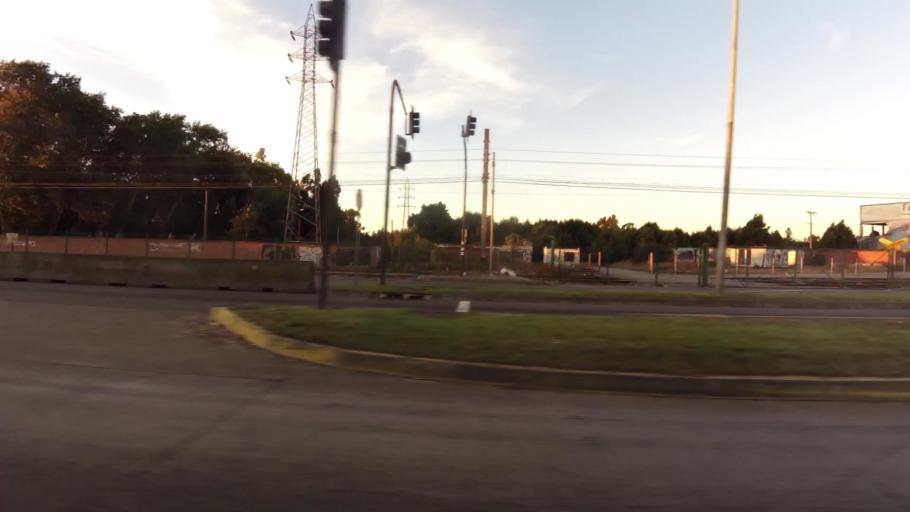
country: CL
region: Biobio
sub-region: Provincia de Concepcion
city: Concepcion
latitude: -36.8389
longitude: -73.0925
